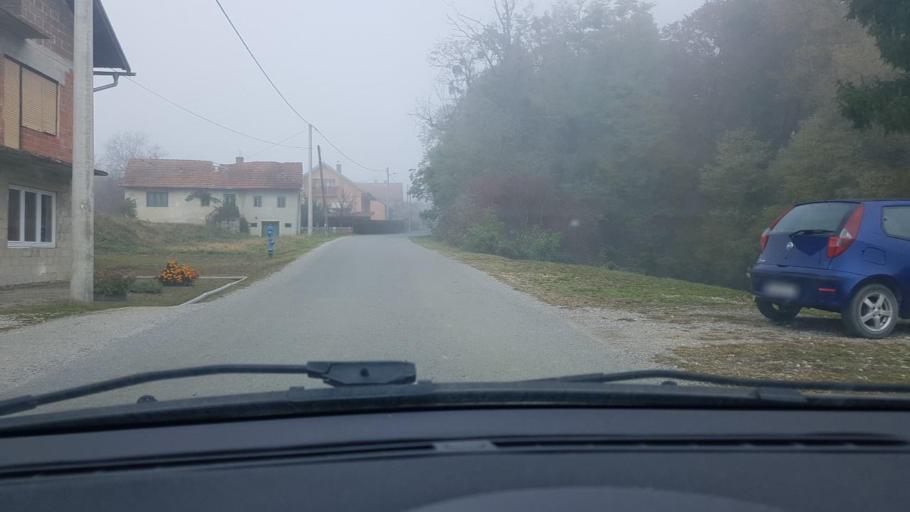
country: HR
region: Krapinsko-Zagorska
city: Mihovljan
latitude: 46.1512
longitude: 15.9902
